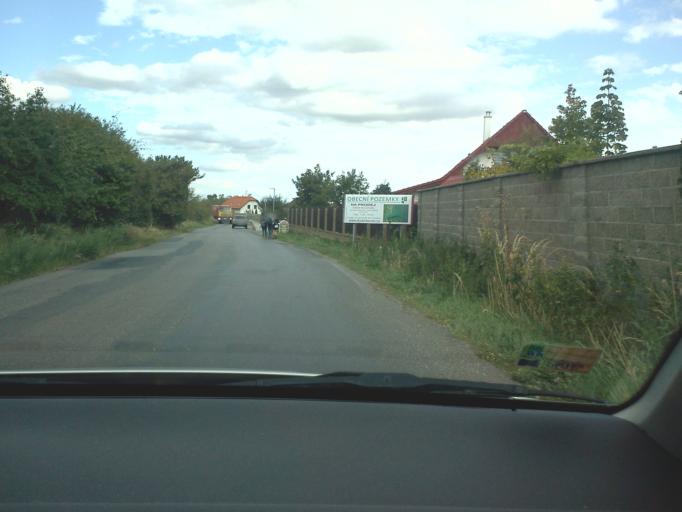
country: CZ
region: Central Bohemia
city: Mukarov
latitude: 50.0180
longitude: 14.7861
